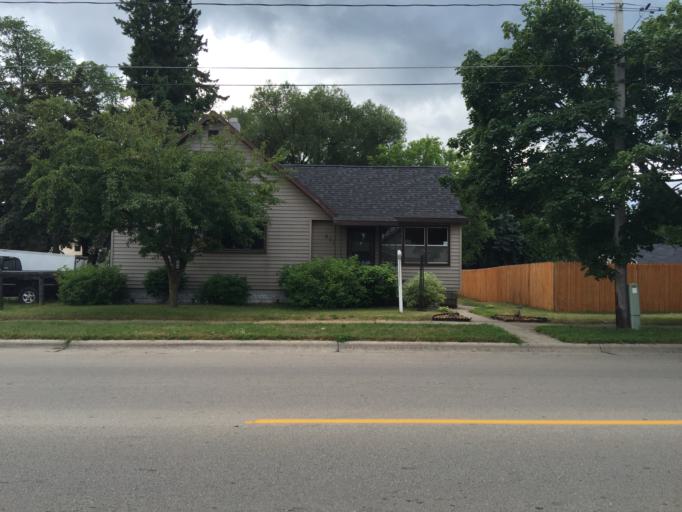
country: US
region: Wisconsin
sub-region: Marinette County
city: Marinette
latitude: 45.0856
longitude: -87.6152
